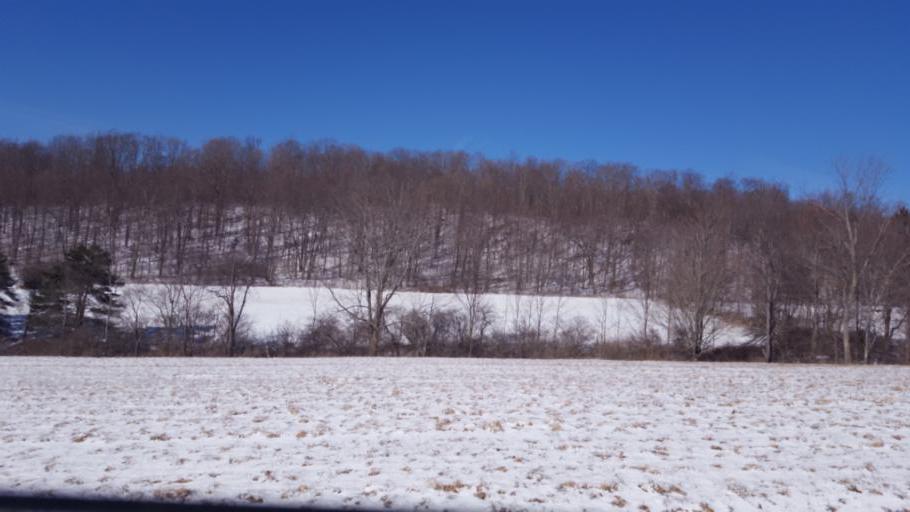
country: US
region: New York
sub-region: Allegany County
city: Wellsville
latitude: 42.1393
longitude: -77.9318
